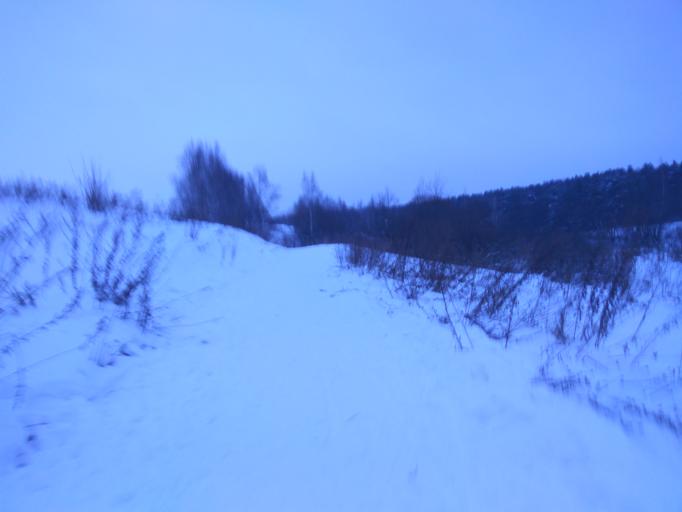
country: RU
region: Moscow
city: Orekhovo-Borisovo Severnoye
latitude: 55.6021
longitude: 37.7008
